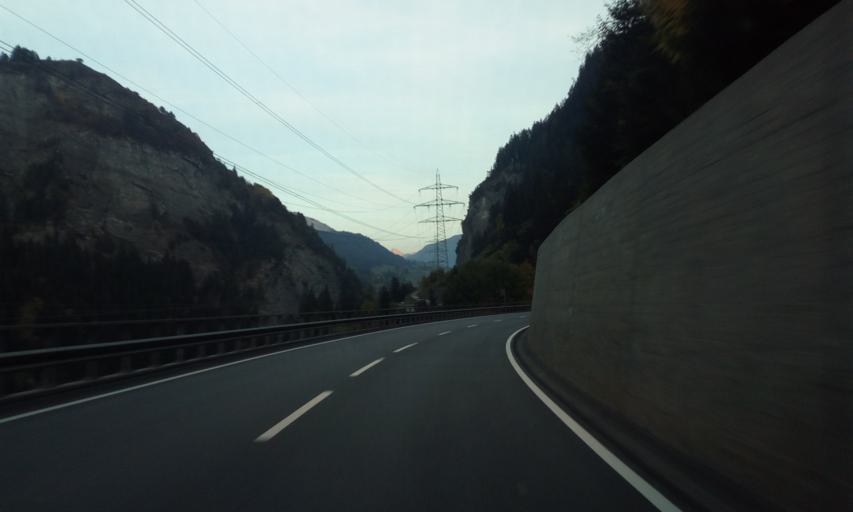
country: CH
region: Grisons
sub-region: Hinterrhein District
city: Thusis
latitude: 46.6871
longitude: 9.5046
